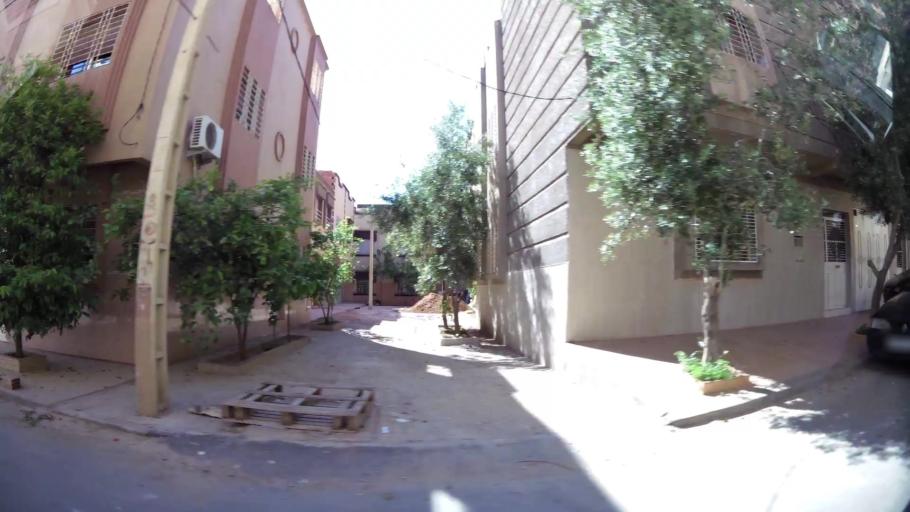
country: MA
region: Oriental
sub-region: Oujda-Angad
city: Oujda
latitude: 34.6581
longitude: -1.9186
